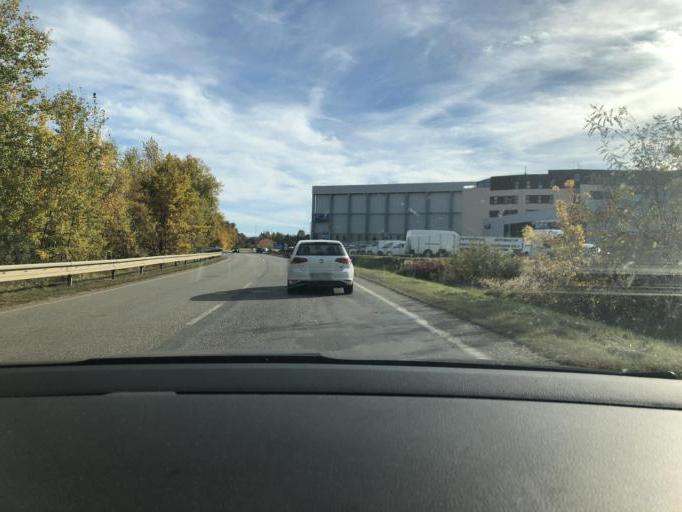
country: CZ
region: Central Bohemia
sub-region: Okres Benesov
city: Benesov
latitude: 49.7856
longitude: 14.6997
